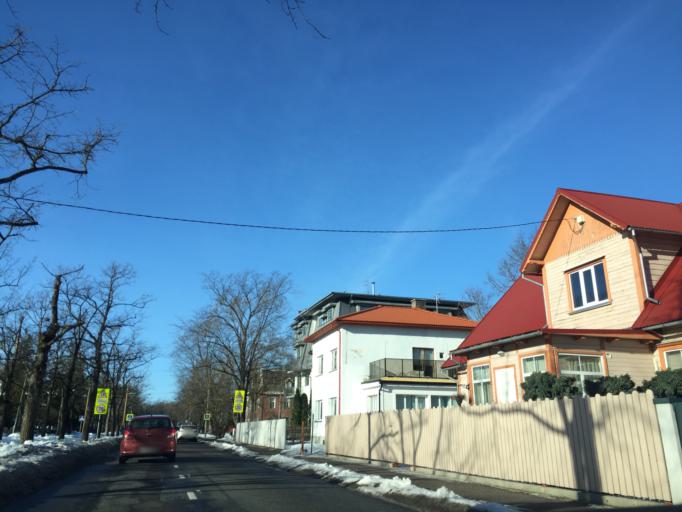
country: EE
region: Paernumaa
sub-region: Paernu linn
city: Parnu
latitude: 58.3764
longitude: 24.5047
